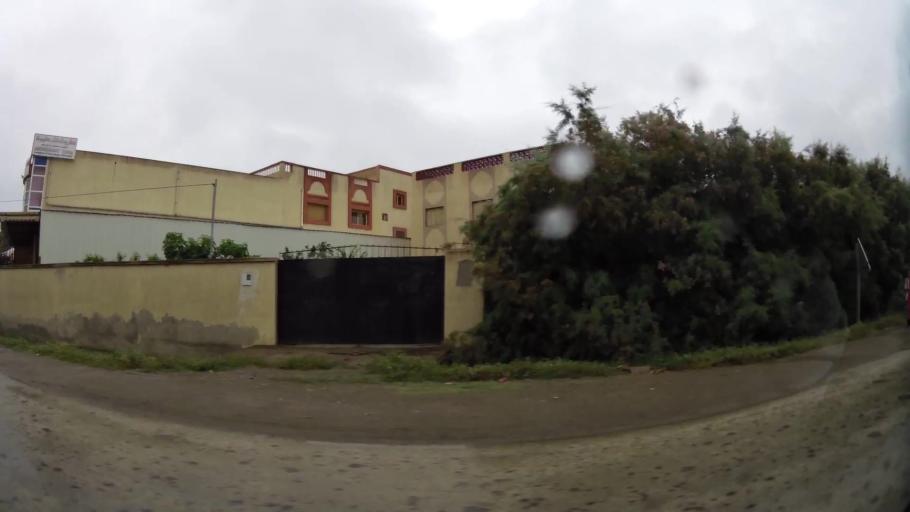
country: MA
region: Taza-Al Hoceima-Taounate
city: Imzourene
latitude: 35.1549
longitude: -3.8363
